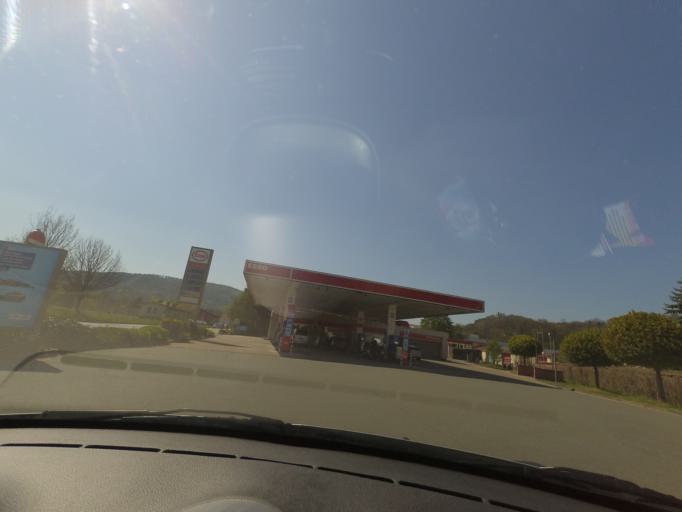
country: DE
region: Thuringia
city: Bad Blankenburg
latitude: 50.6836
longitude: 11.2790
